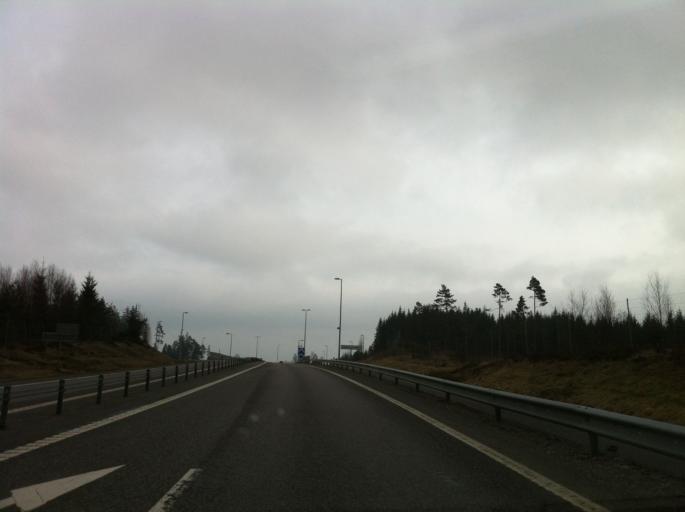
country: SE
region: Vaestra Goetaland
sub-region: Boras Kommun
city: Dalsjofors
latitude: 57.7638
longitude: 13.1135
